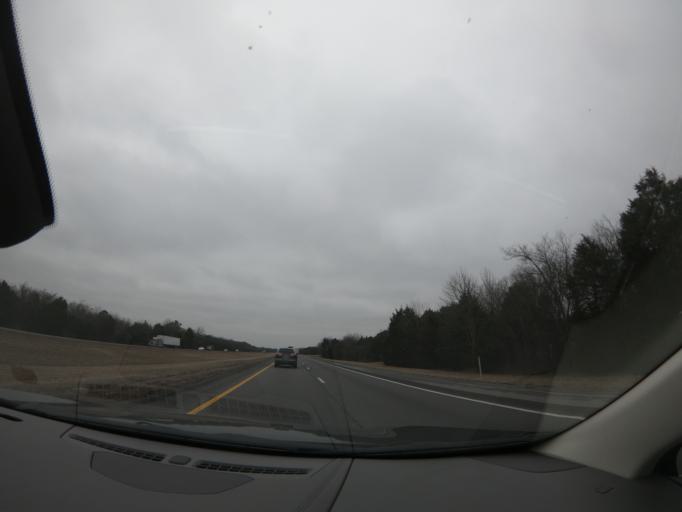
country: US
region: Tennessee
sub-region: Rutherford County
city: Plainview
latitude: 35.6818
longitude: -86.2889
